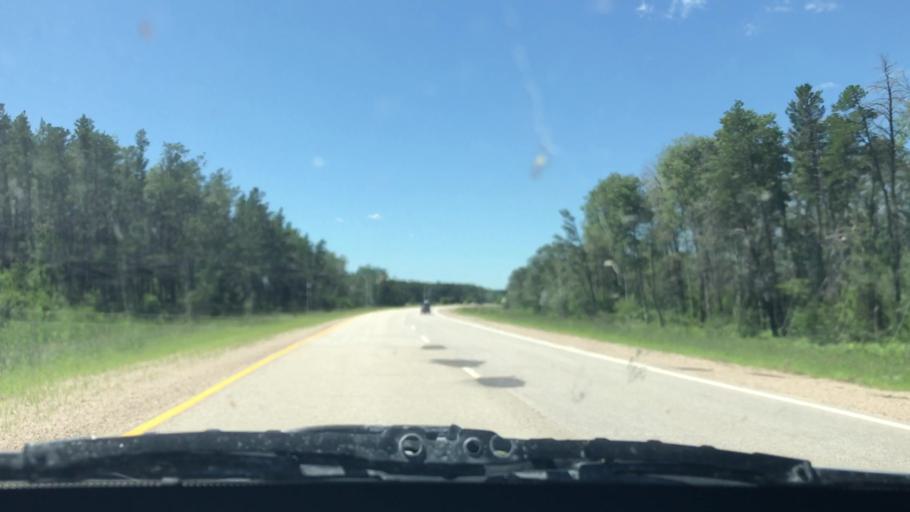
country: CA
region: Manitoba
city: La Broquerie
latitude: 49.6570
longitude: -96.1455
